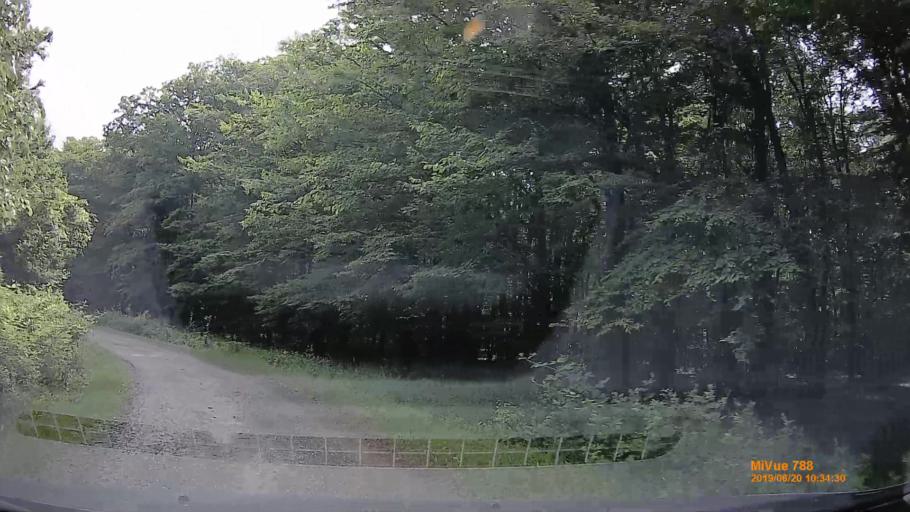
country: HU
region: Baranya
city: Mecseknadasd
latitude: 46.1975
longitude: 18.5188
